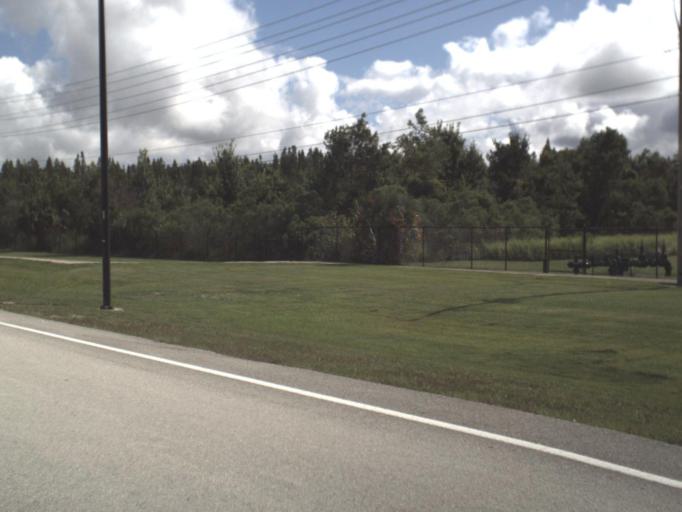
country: US
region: Florida
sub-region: Polk County
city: Winston
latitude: 28.0057
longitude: -82.0176
